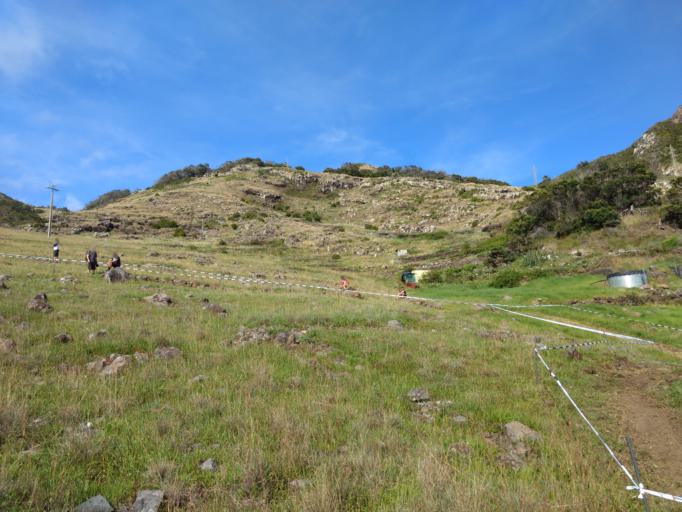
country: PT
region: Madeira
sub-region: Machico
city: Machico
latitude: 32.7255
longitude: -16.7643
